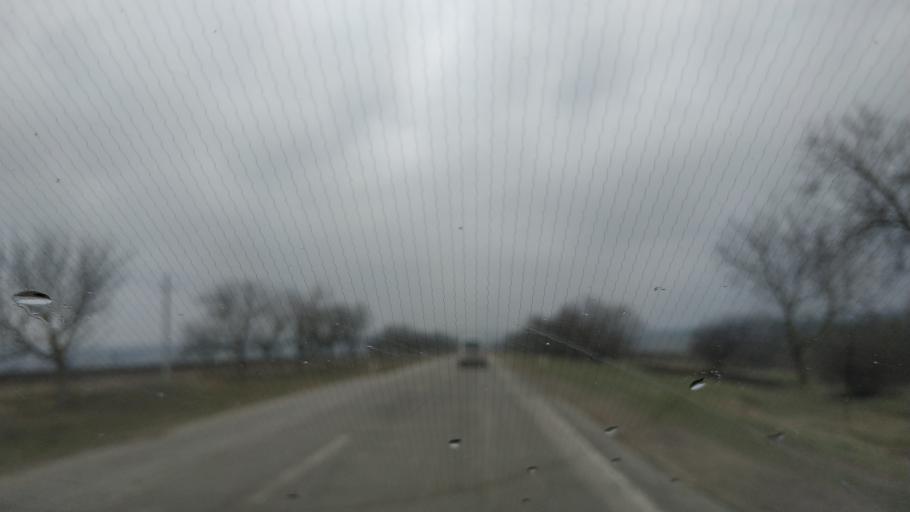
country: MD
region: Gagauzia
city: Comrat
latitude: 46.2526
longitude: 28.7565
